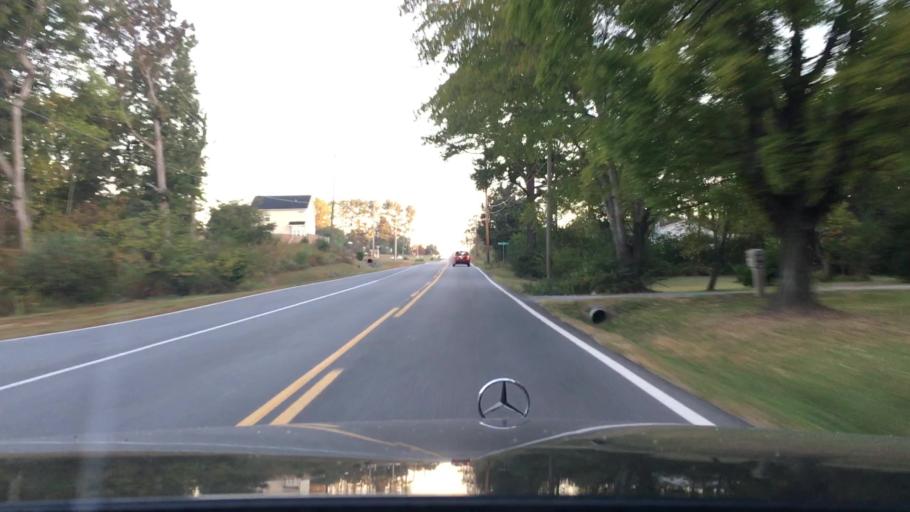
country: US
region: Virginia
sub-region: Campbell County
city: Timberlake
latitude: 37.3058
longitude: -79.2347
